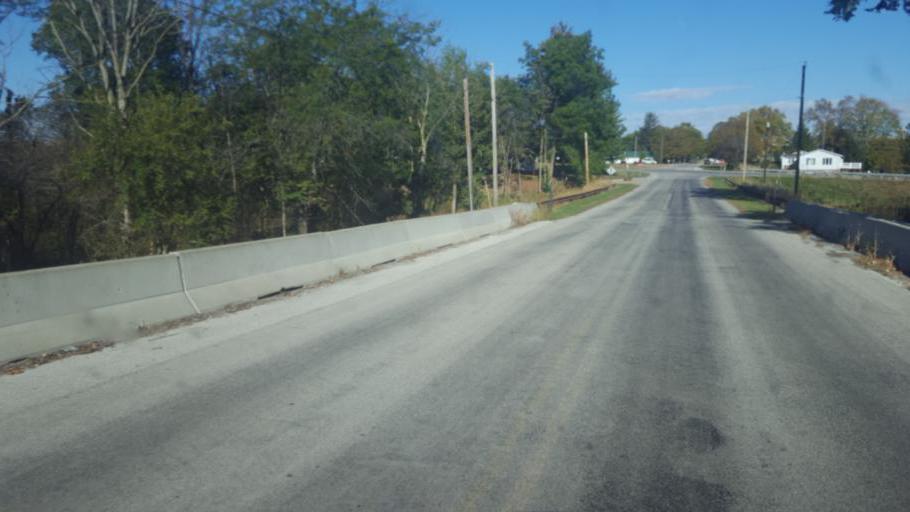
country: US
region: Ohio
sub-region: Wyandot County
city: Upper Sandusky
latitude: 40.7375
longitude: -83.2139
